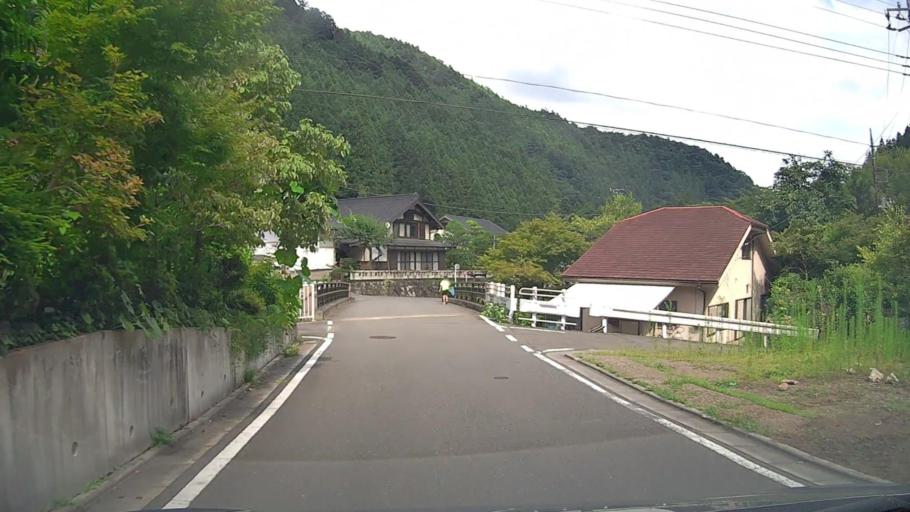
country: JP
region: Tokyo
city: Itsukaichi
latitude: 35.7472
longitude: 139.1195
